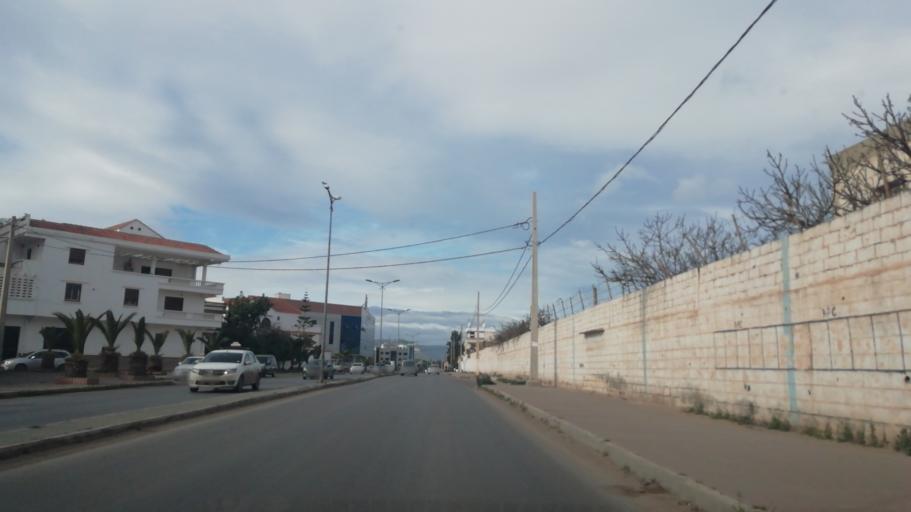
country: DZ
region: Oran
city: Bir el Djir
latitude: 35.7126
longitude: -0.5938
